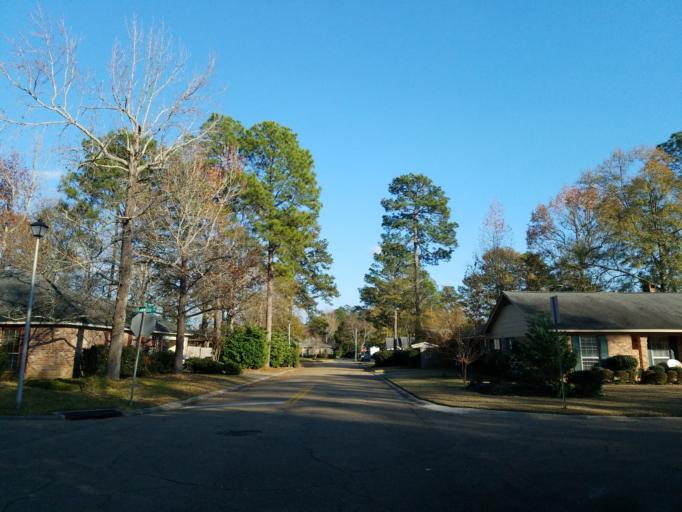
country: US
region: Mississippi
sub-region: Lamar County
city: West Hattiesburg
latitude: 31.3050
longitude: -89.3370
